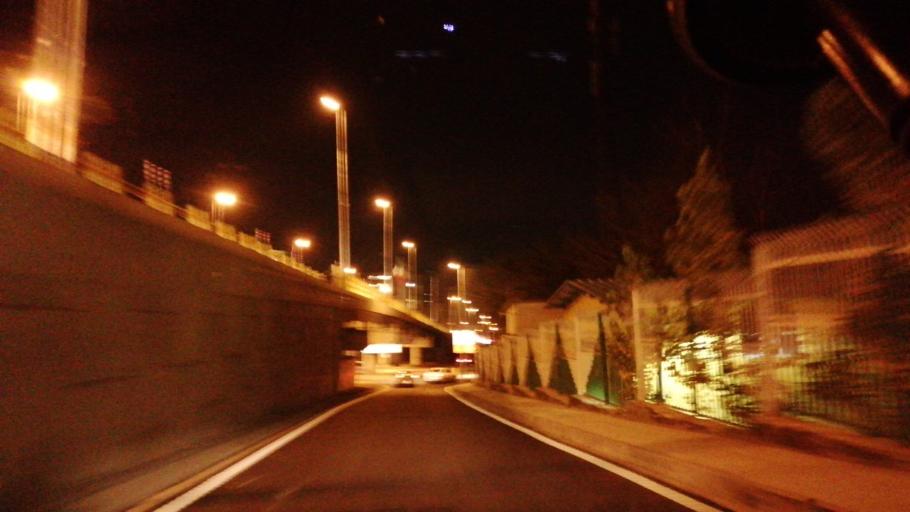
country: IR
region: Tehran
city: Tajrish
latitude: 35.7923
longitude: 51.4877
